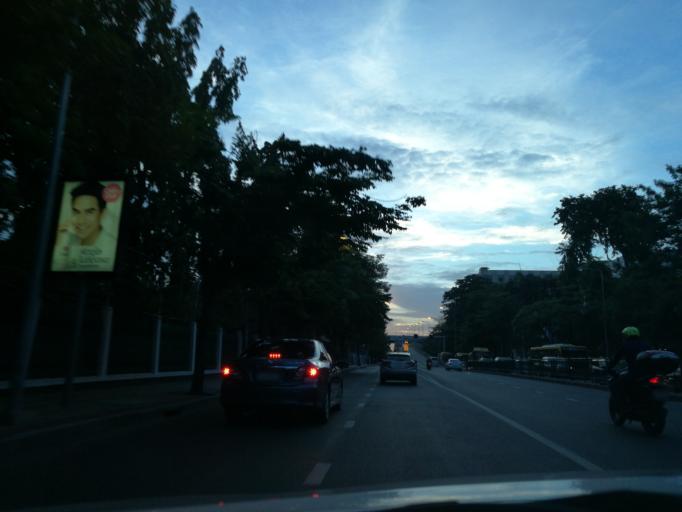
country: TH
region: Bangkok
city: Ratchathewi
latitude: 13.7678
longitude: 100.5325
